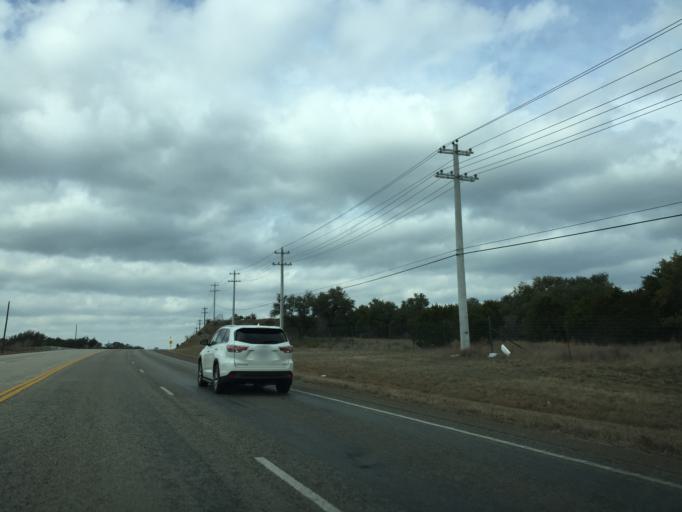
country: US
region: Texas
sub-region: Travis County
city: Briarcliff
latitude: 30.4053
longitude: -98.1010
